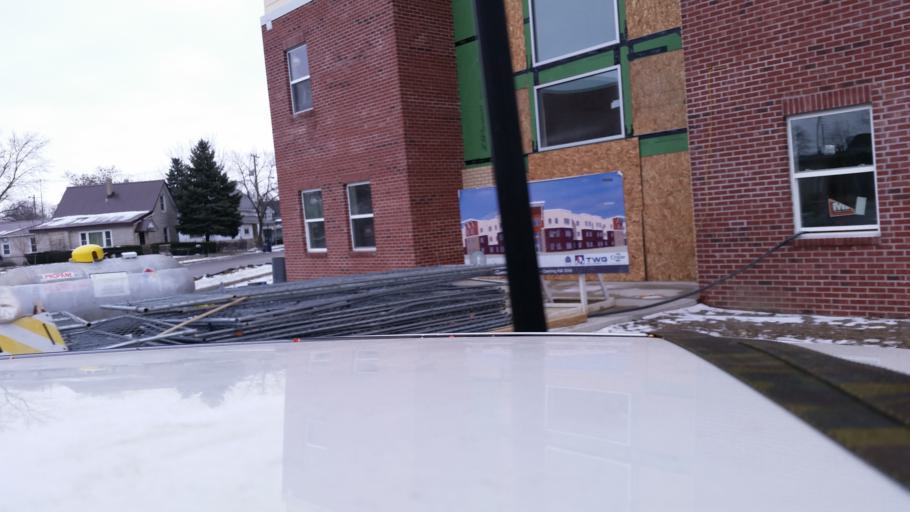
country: US
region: Indiana
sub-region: Howard County
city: Kokomo
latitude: 40.4908
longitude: -86.1268
